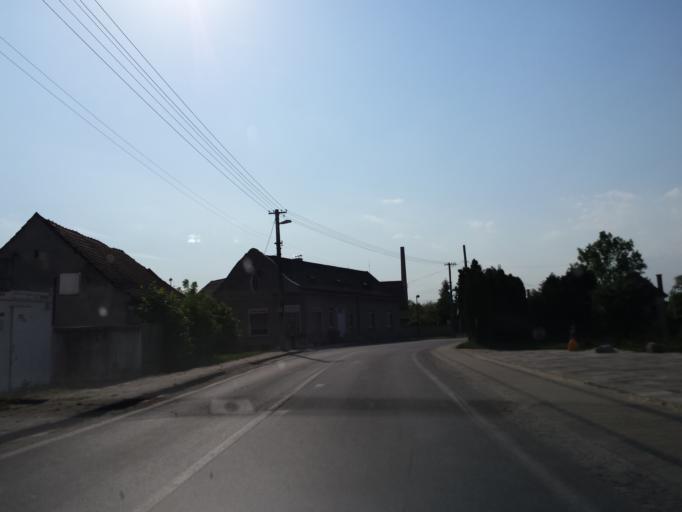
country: AT
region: Lower Austria
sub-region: Politischer Bezirk Ganserndorf
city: Angern an der March
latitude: 48.3809
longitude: 16.8446
